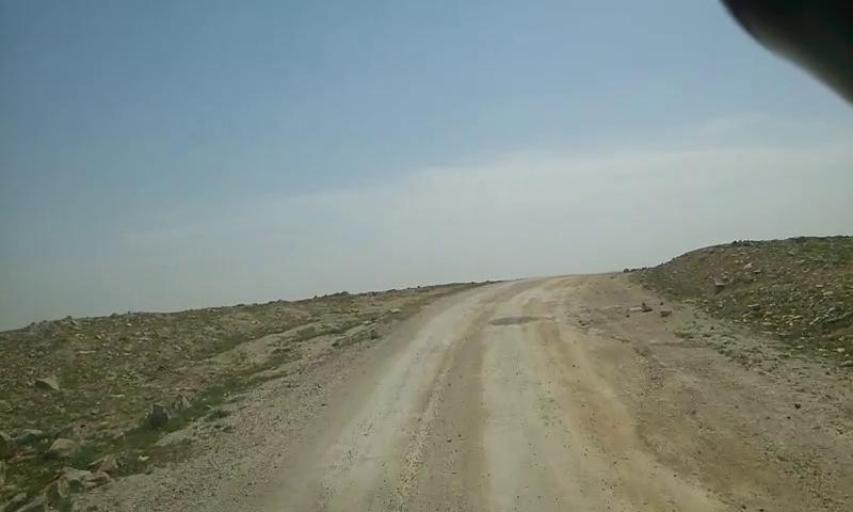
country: PS
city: `Arab ar Rashaydah
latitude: 31.5195
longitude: 35.2967
